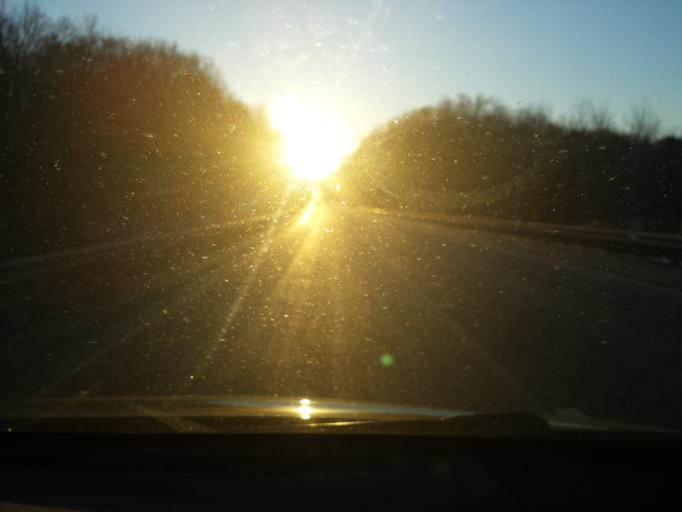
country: US
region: Pennsylvania
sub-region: Clinton County
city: Mill Hall
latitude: 41.0262
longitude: -77.5583
